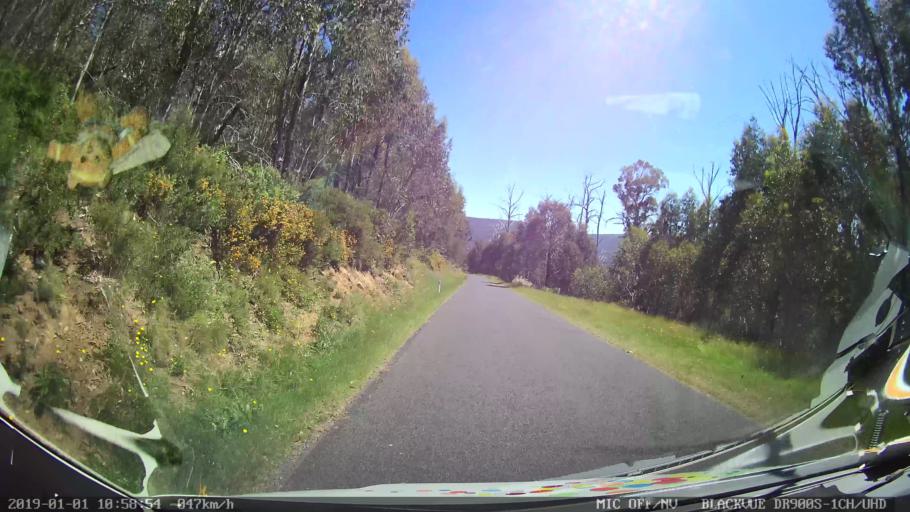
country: AU
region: New South Wales
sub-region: Snowy River
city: Jindabyne
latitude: -35.9891
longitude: 148.3985
